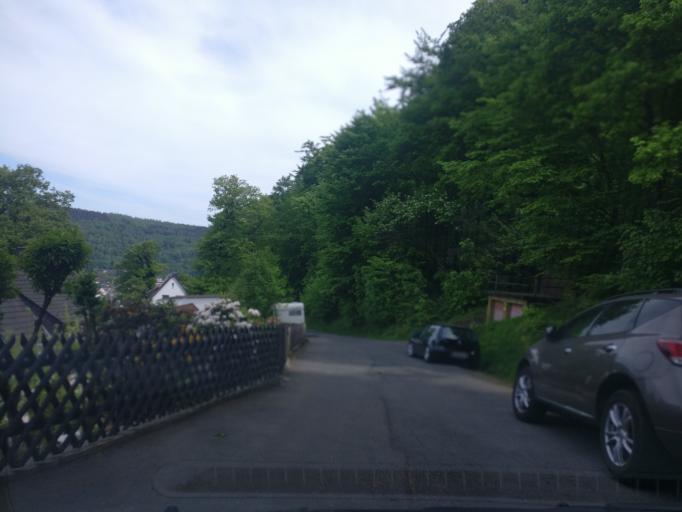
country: DE
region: Lower Saxony
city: Hannoversch Munden
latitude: 51.4115
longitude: 9.6646
